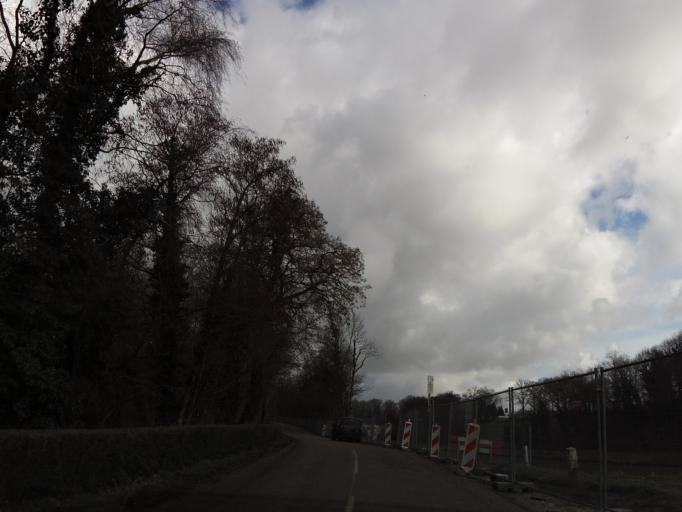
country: NL
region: Limburg
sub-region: Gemeente Stein
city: Elsloo
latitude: 50.9490
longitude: 5.7576
